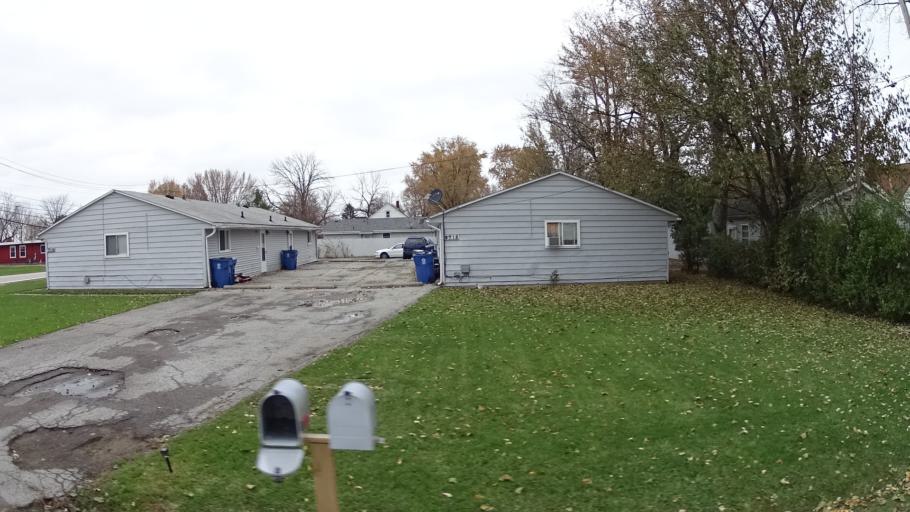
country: US
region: Ohio
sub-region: Lorain County
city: Amherst
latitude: 41.4418
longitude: -82.2277
